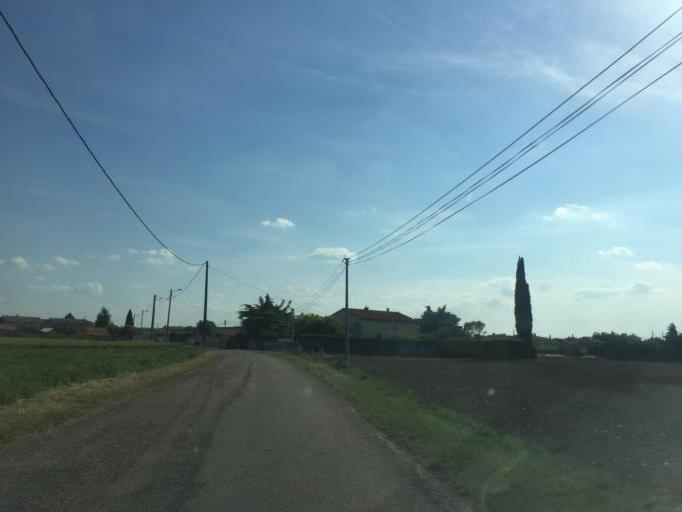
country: FR
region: Rhone-Alpes
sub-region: Departement de la Drome
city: Pierrelatte
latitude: 44.3868
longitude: 4.7088
